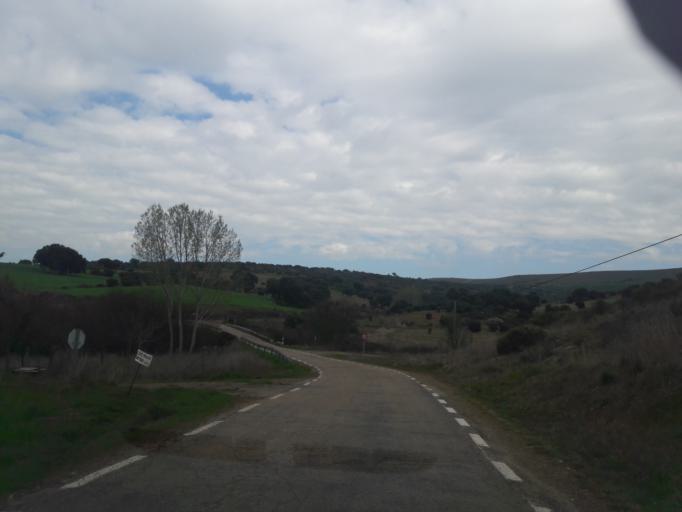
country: ES
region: Castille and Leon
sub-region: Provincia de Salamanca
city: Serradilla del Arroyo
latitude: 40.5218
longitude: -6.3724
